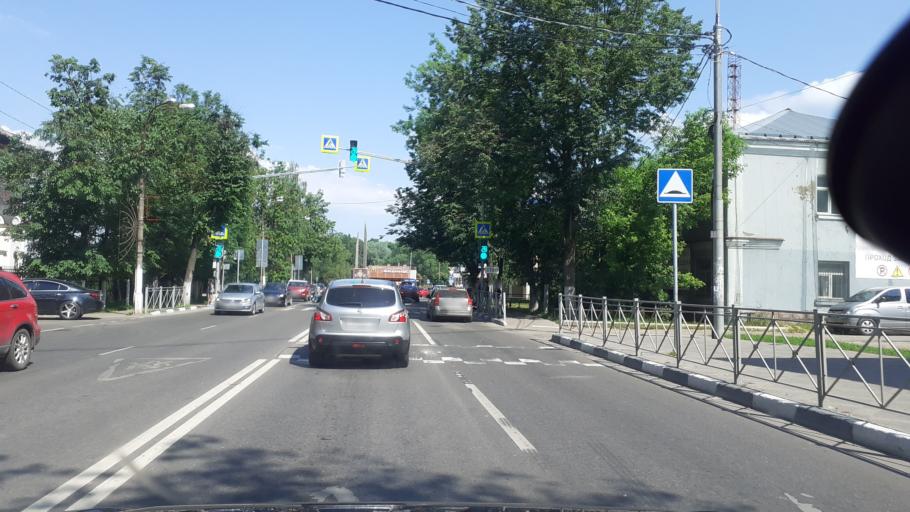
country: RU
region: Moskovskaya
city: Naro-Fominsk
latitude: 55.3868
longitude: 36.7405
